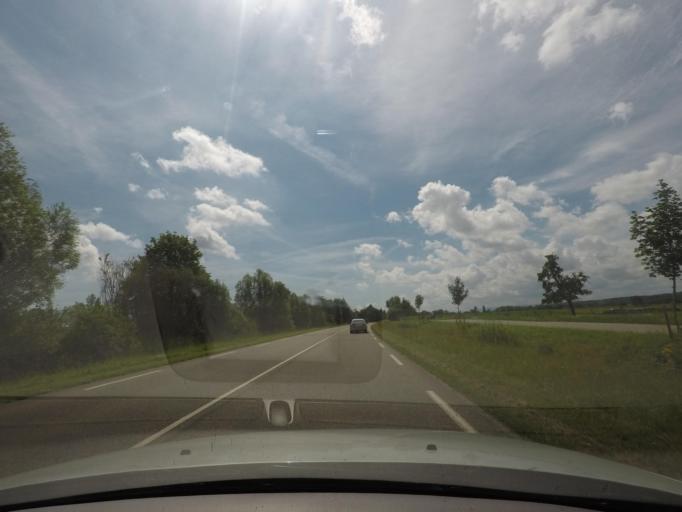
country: FR
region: Alsace
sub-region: Departement du Bas-Rhin
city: Drulingen
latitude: 48.8549
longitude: 7.2021
